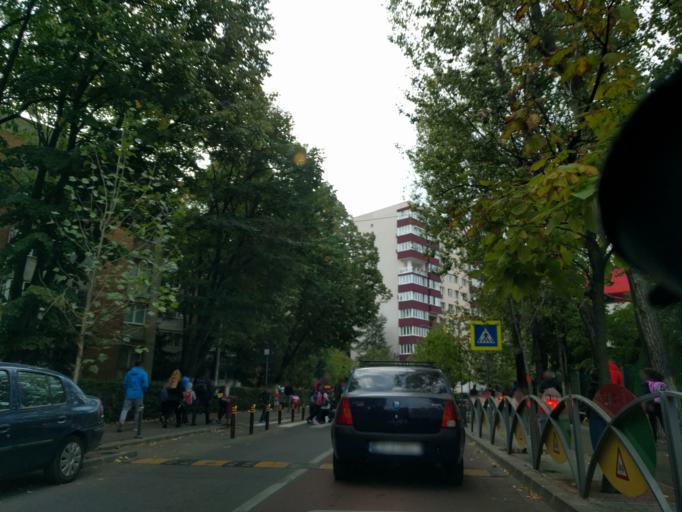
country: RO
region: Ilfov
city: Dobroesti
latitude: 44.4219
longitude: 26.1615
